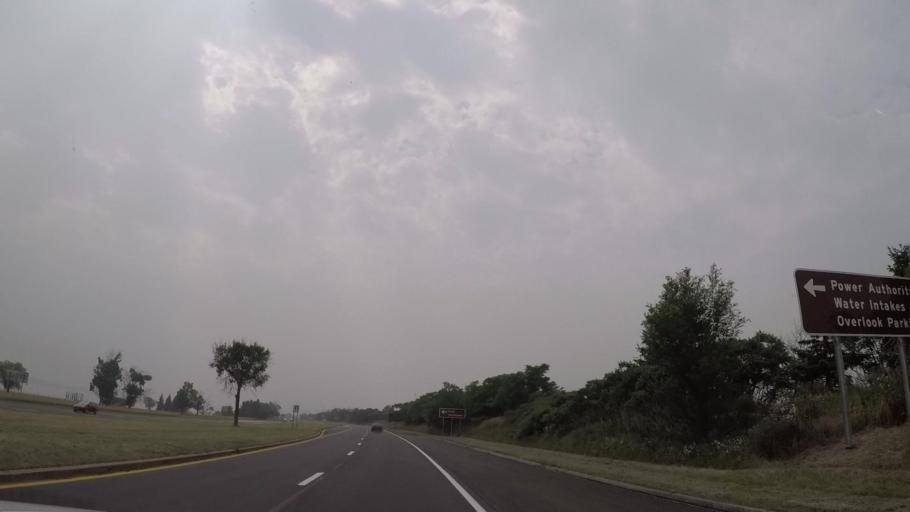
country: US
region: New York
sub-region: Niagara County
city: Niagara Falls
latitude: 43.0785
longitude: -79.0161
